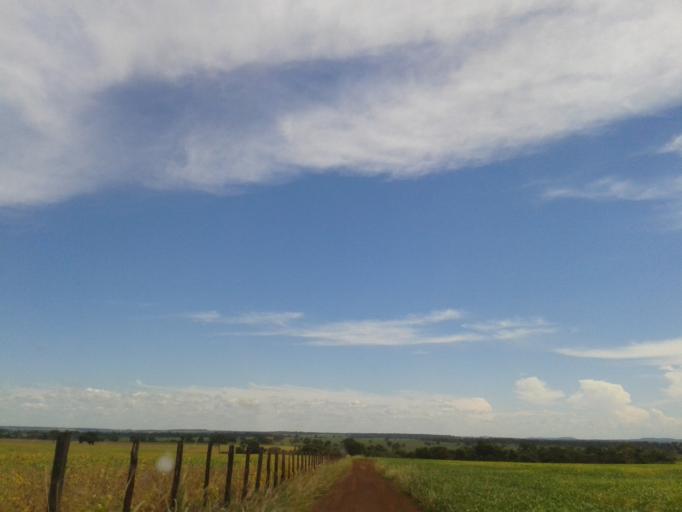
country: BR
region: Minas Gerais
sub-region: Capinopolis
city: Capinopolis
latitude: -18.7711
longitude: -49.7970
